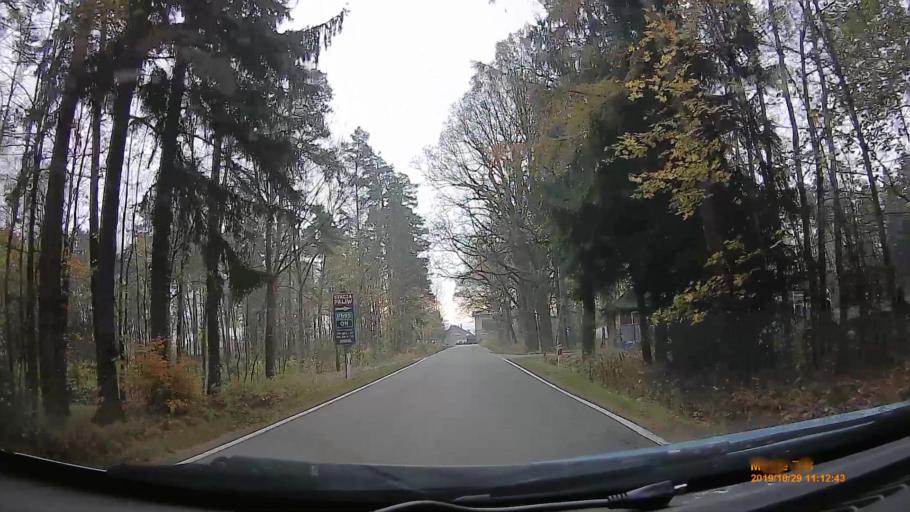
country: PL
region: Lower Silesian Voivodeship
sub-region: Powiat klodzki
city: Polanica-Zdroj
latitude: 50.4249
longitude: 16.5055
